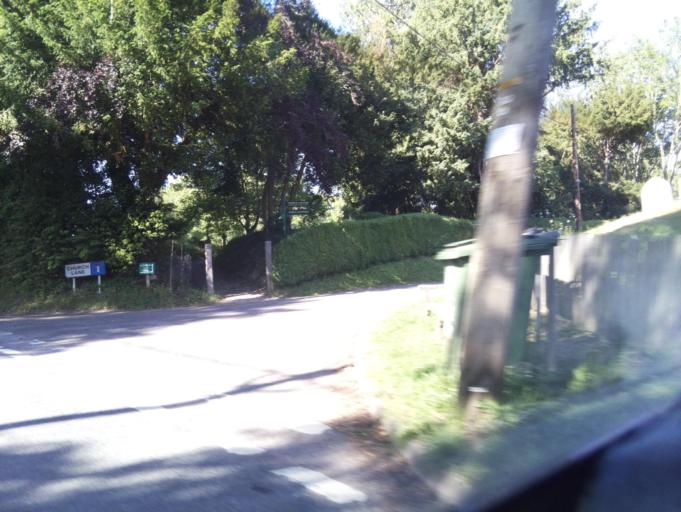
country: GB
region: England
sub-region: Hampshire
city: Winchester
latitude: 51.0938
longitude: -1.3540
